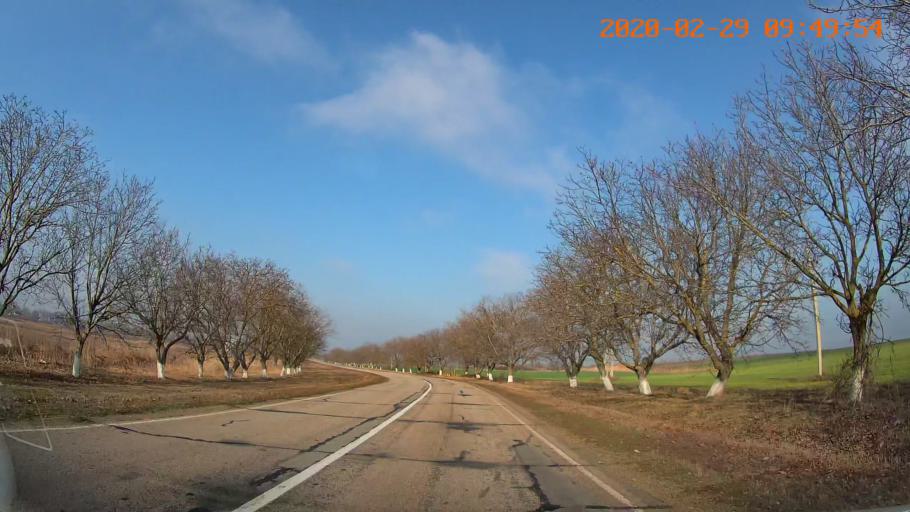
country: MD
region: Telenesti
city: Crasnoe
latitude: 46.7003
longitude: 29.7652
